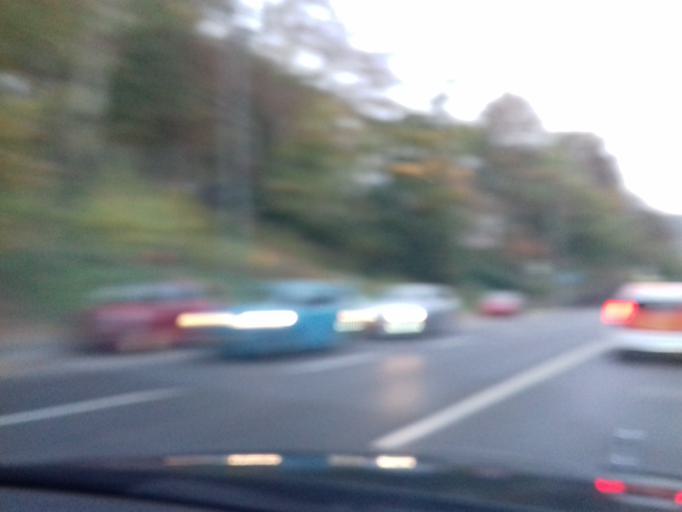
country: LU
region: Luxembourg
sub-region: Canton de Luxembourg
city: Luxembourg
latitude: 49.6204
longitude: 6.1304
